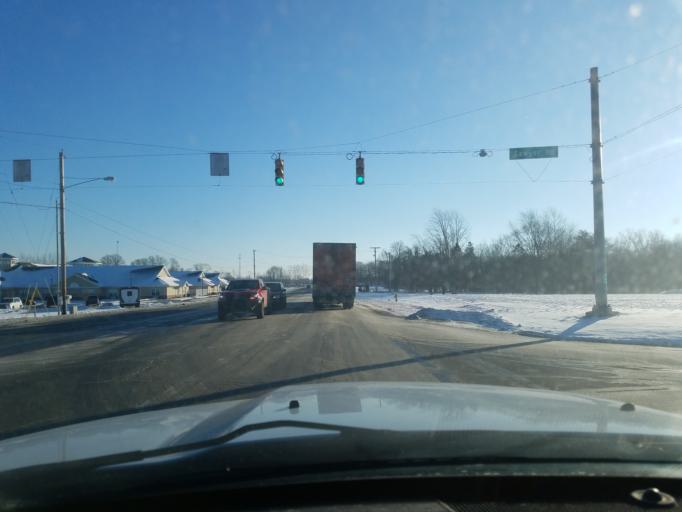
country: US
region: Indiana
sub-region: Noble County
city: Kendallville
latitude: 41.4523
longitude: -85.2940
